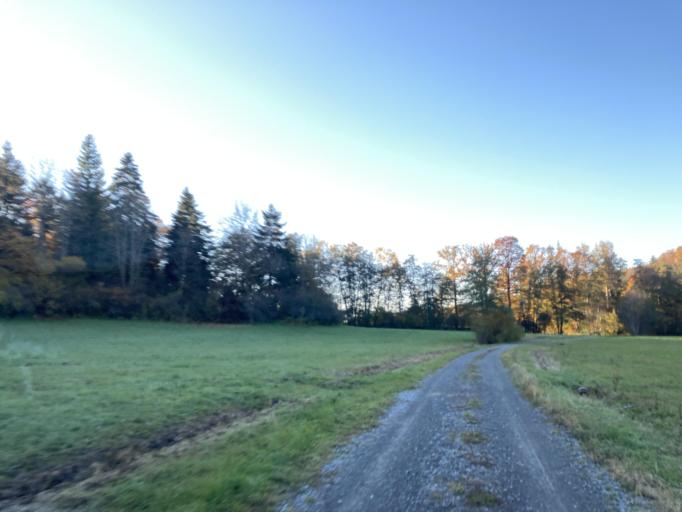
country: DE
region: Baden-Wuerttemberg
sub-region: Tuebingen Region
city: Bodelshausen
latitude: 48.4277
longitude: 8.9663
